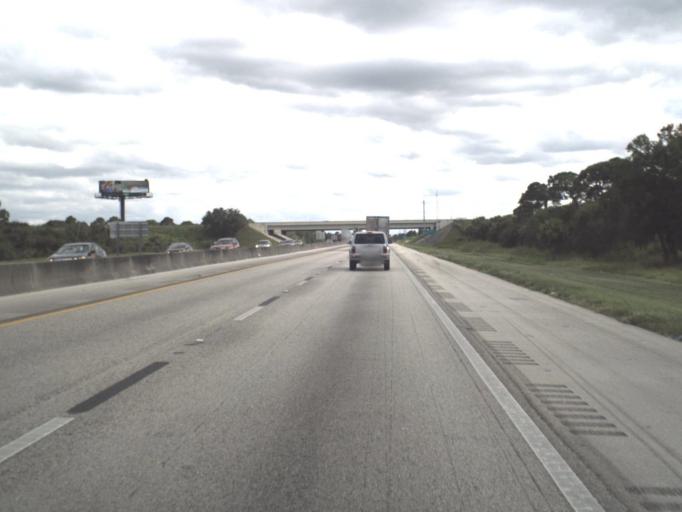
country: US
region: Florida
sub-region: Saint Lucie County
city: Fort Pierce South
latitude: 27.3985
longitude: -80.3959
